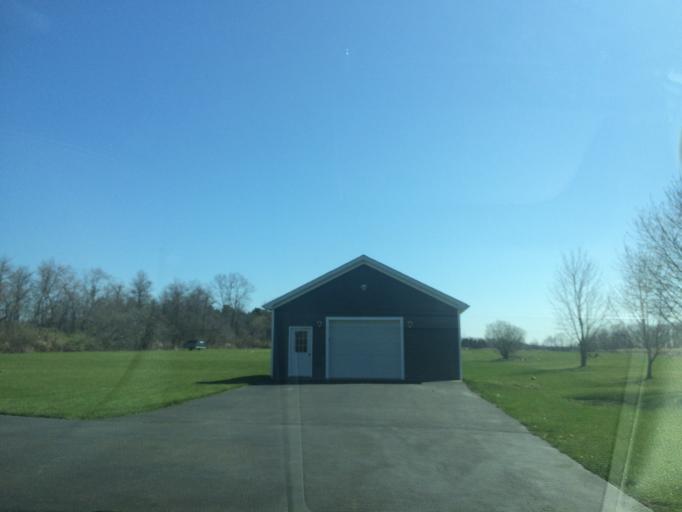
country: US
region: New York
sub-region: Wayne County
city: Palmyra
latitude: 43.0681
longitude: -77.2599
